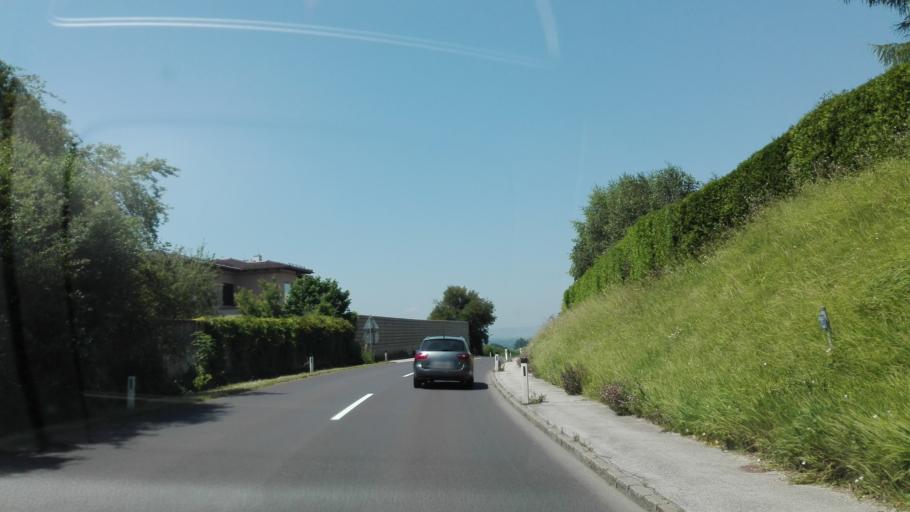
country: AT
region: Upper Austria
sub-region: Politischer Bezirk Linz-Land
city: Pasching
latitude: 48.2773
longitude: 14.1646
